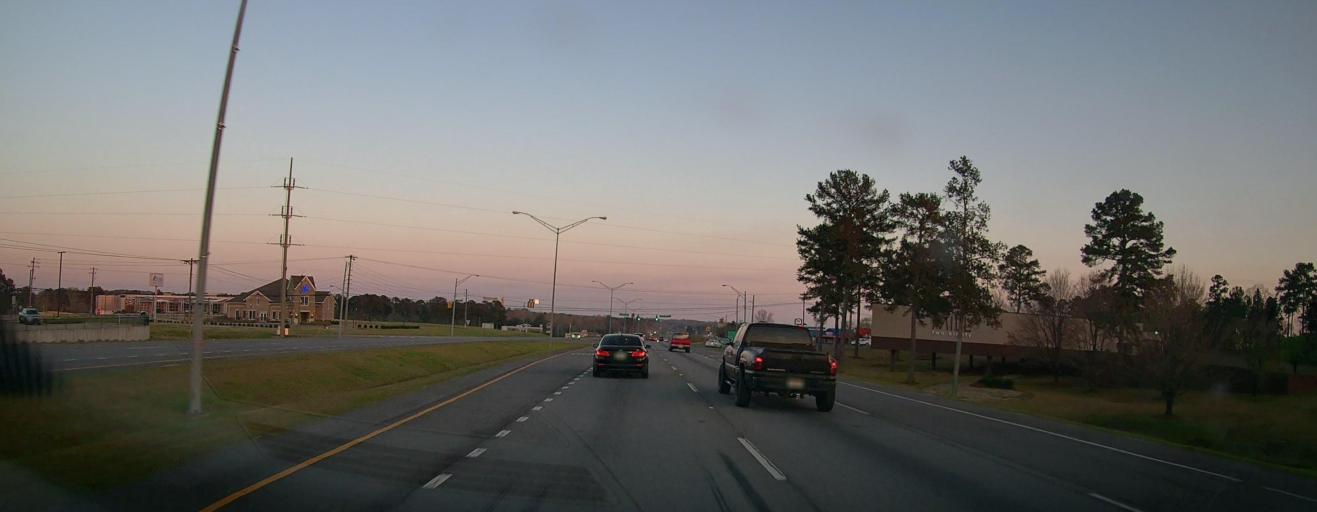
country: US
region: Alabama
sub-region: Tallapoosa County
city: Alexander City
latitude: 32.9298
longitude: -85.9669
